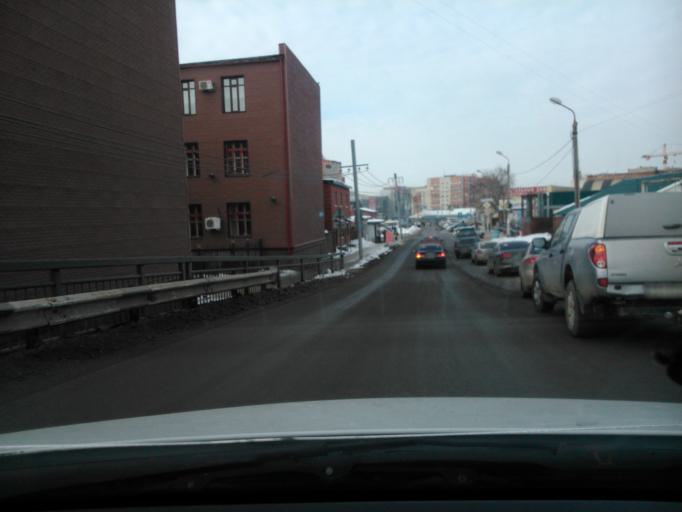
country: RU
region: Perm
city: Perm
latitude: 58.0004
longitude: 56.2262
